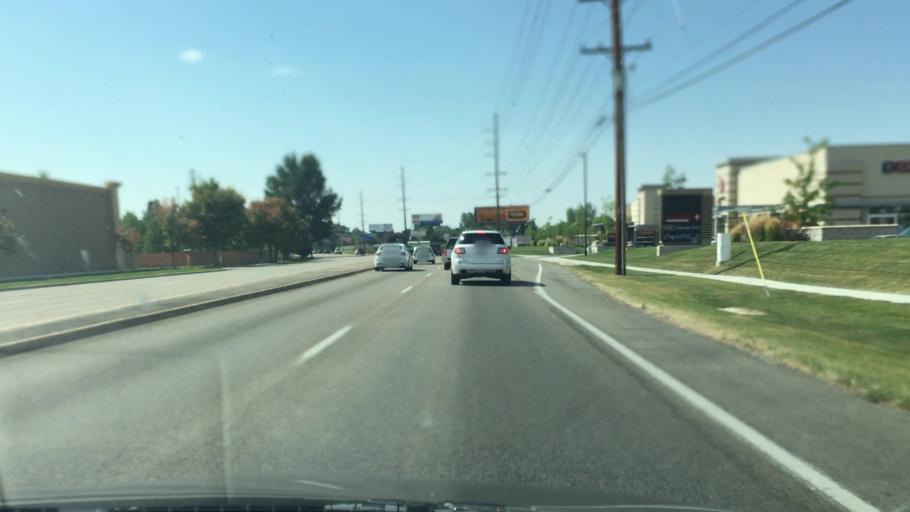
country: US
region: Idaho
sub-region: Ada County
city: Garden City
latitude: 43.6707
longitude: -116.2826
